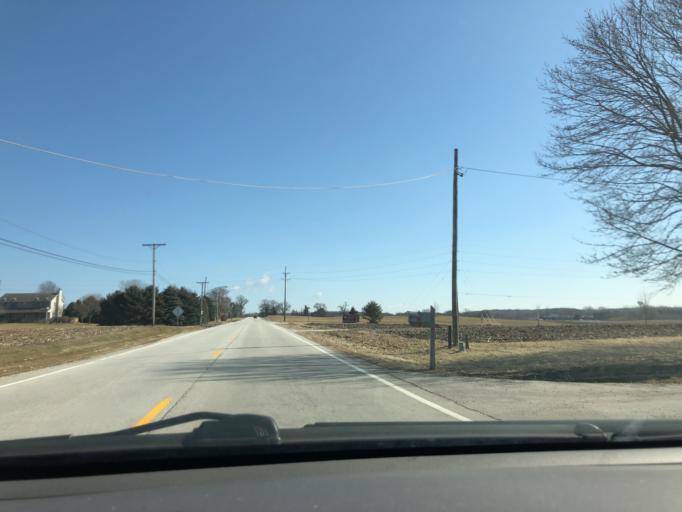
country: US
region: Illinois
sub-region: Kane County
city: Hampshire
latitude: 42.1065
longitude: -88.5233
